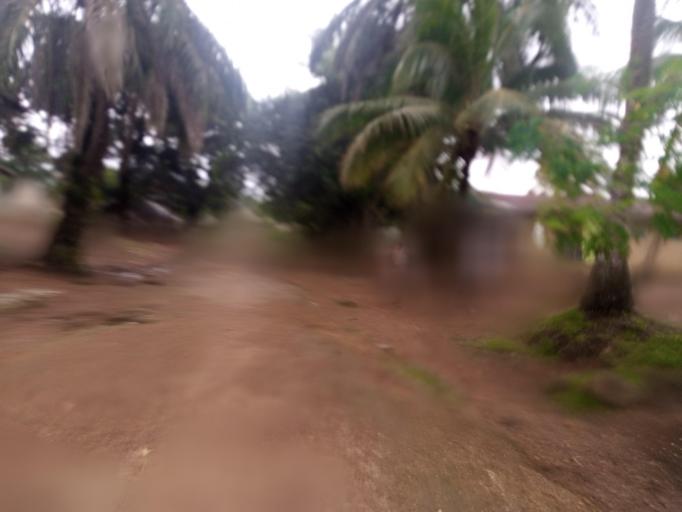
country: SL
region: Eastern Province
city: Kenema
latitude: 7.8611
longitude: -11.1932
